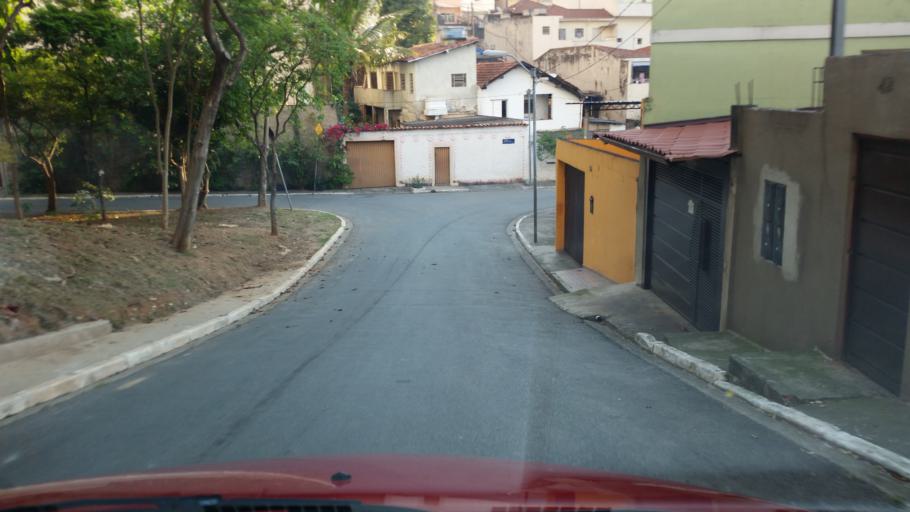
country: BR
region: Sao Paulo
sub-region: Sao Paulo
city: Sao Paulo
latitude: -23.6048
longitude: -46.6226
